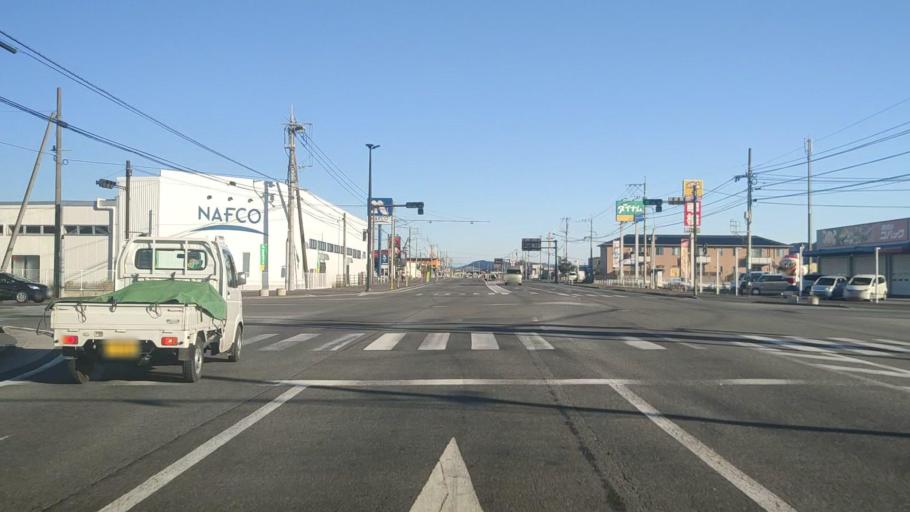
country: JP
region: Miyazaki
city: Nobeoka
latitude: 32.3967
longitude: 131.6294
